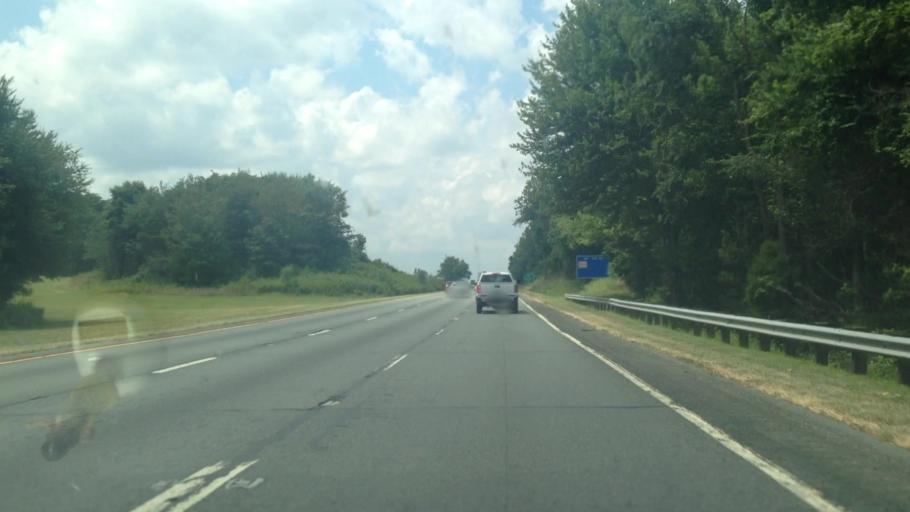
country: US
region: North Carolina
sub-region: Forsyth County
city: Rural Hall
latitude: 36.2057
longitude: -80.2976
